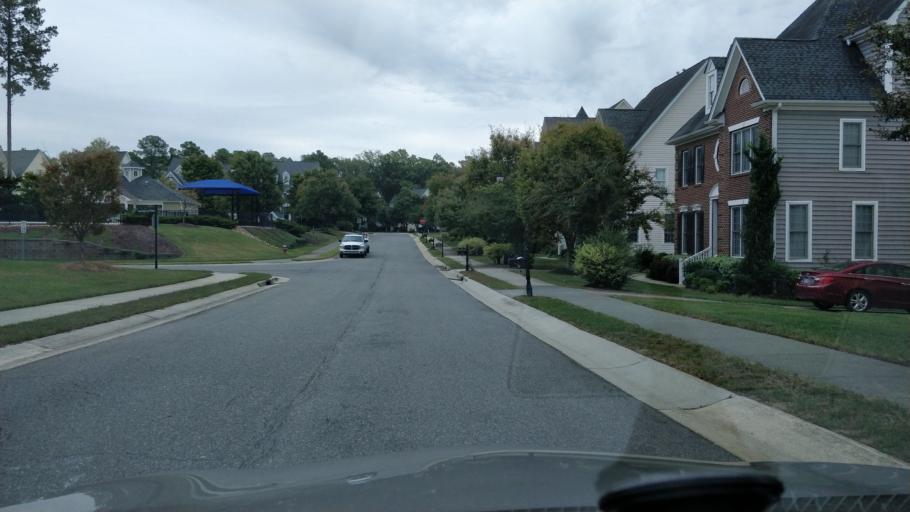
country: US
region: North Carolina
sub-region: Wake County
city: Morrisville
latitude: 35.8196
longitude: -78.8352
